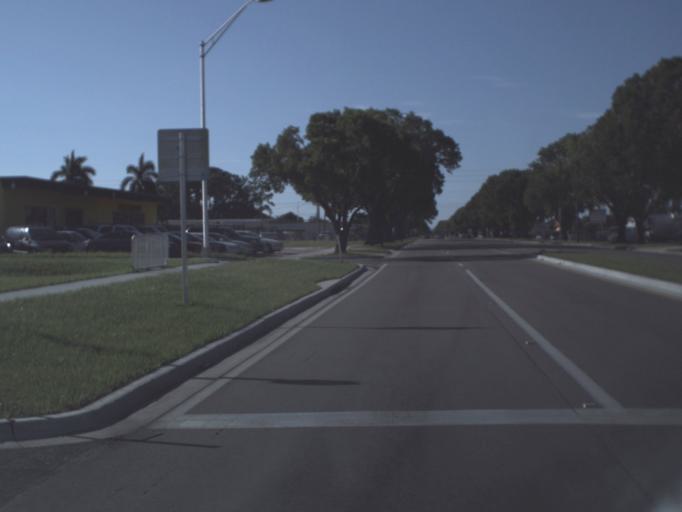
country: US
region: Florida
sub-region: Lee County
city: Fort Myers
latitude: 26.6204
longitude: -81.8620
